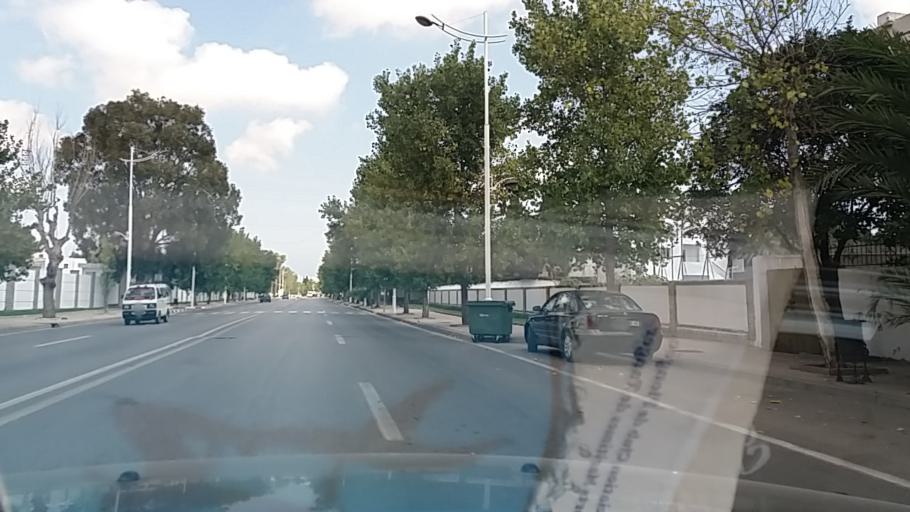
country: MA
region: Tanger-Tetouan
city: Tetouan
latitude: 35.5767
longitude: -5.3407
